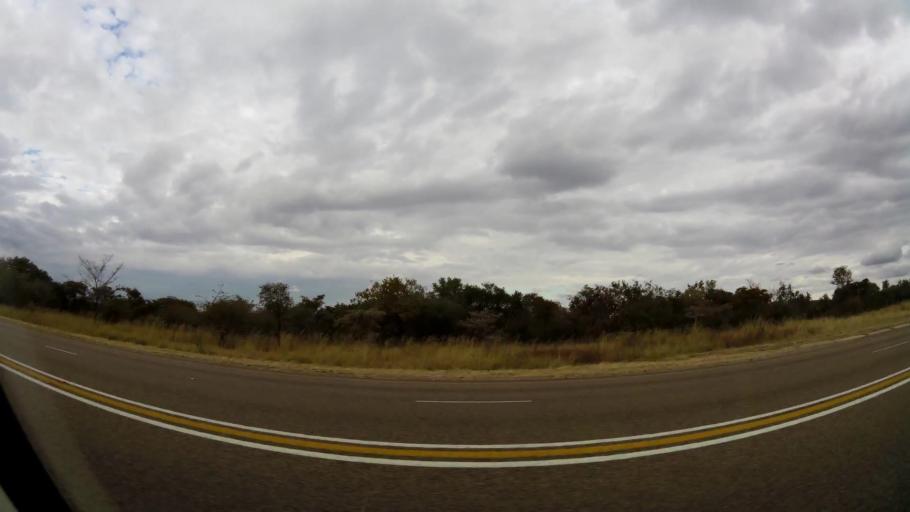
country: ZA
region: Limpopo
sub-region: Waterberg District Municipality
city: Modimolle
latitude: -24.6581
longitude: 28.5812
